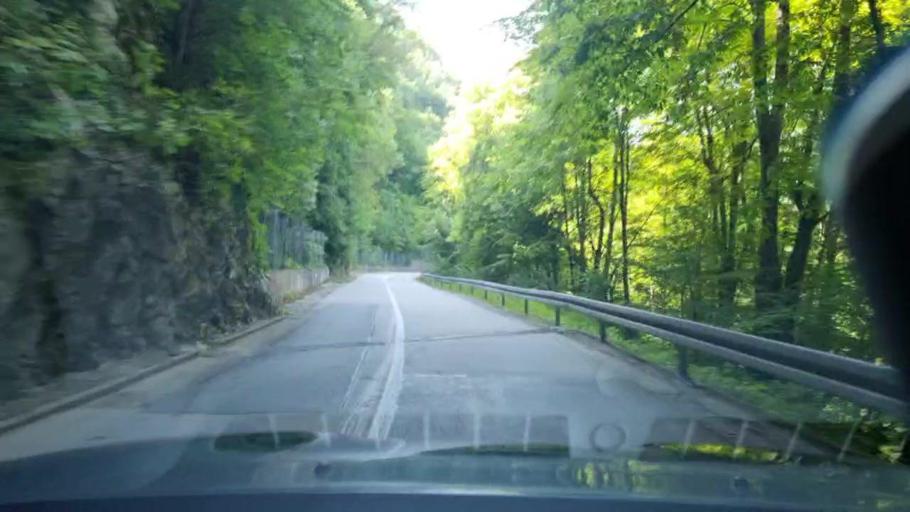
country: BA
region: Federation of Bosnia and Herzegovina
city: Bosanska Krupa
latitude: 44.8753
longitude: 16.0747
